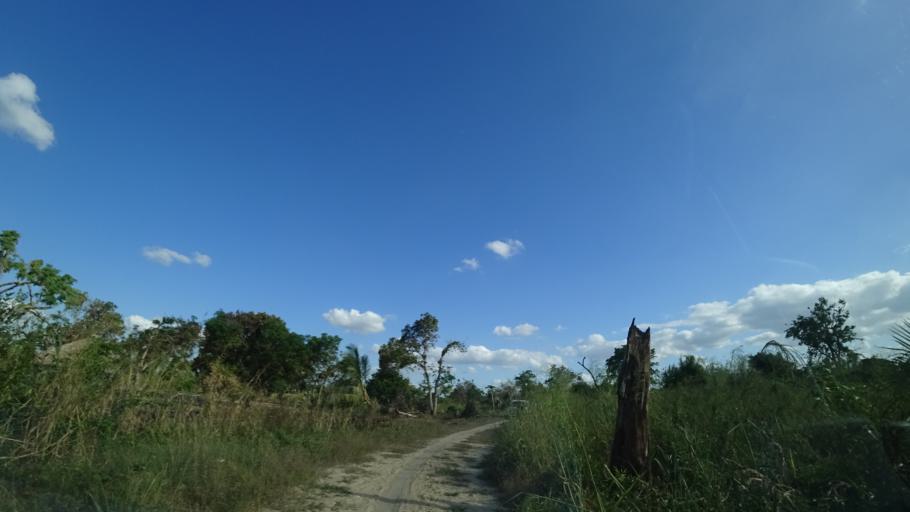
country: MZ
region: Sofala
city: Dondo
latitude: -19.3446
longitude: 34.5822
